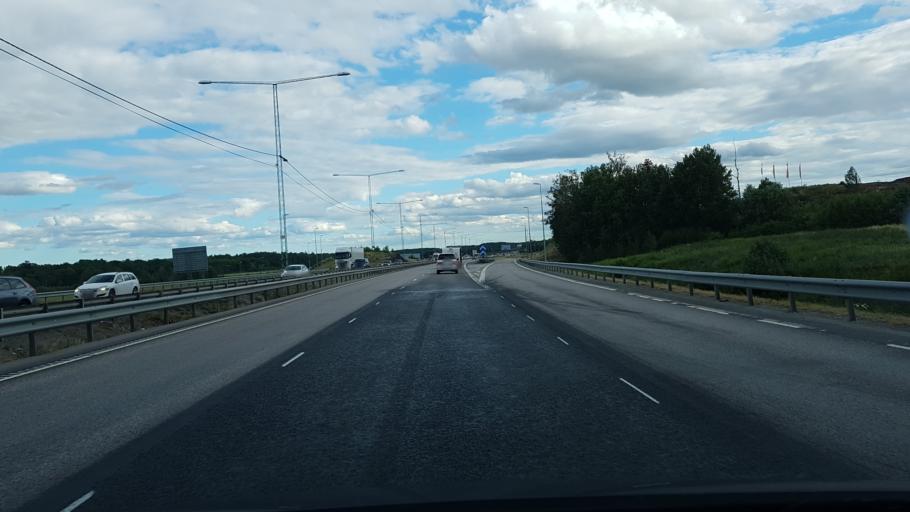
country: SE
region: Stockholm
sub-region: Sigtuna Kommun
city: Rosersberg
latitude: 59.5790
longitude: 17.9004
